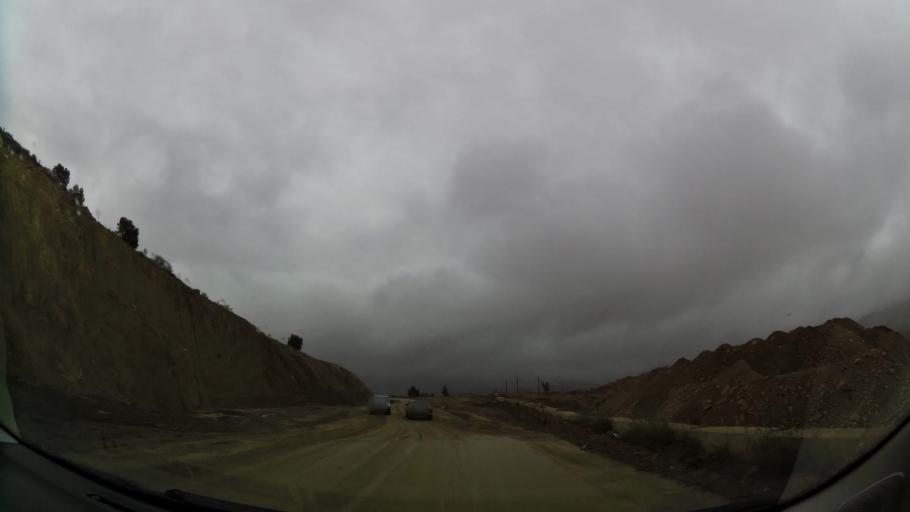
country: MA
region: Oriental
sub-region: Nador
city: Midar
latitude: 34.8972
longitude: -3.7742
